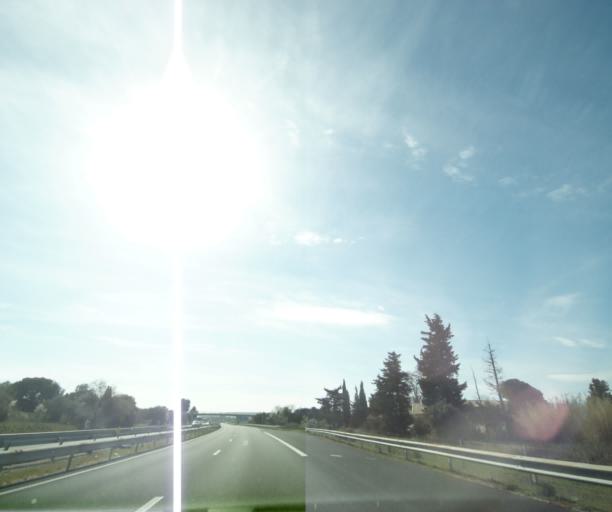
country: FR
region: Provence-Alpes-Cote d'Azur
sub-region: Departement du Vaucluse
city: Caderousse
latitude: 44.1134
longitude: 4.7875
